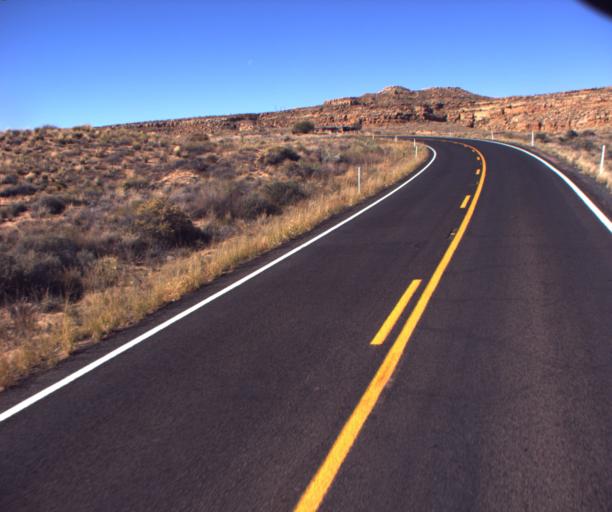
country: US
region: Arizona
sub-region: Navajo County
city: First Mesa
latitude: 35.8827
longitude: -110.6180
